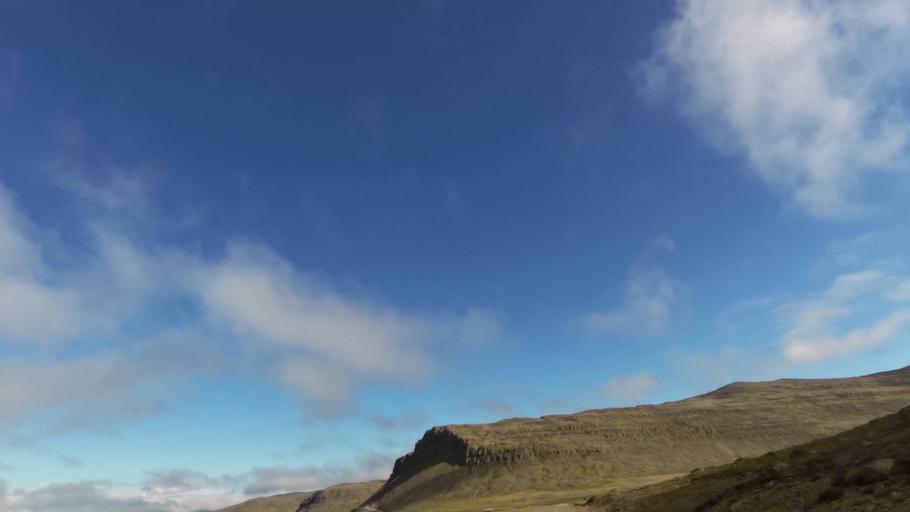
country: IS
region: West
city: Olafsvik
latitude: 65.5756
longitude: -24.0671
